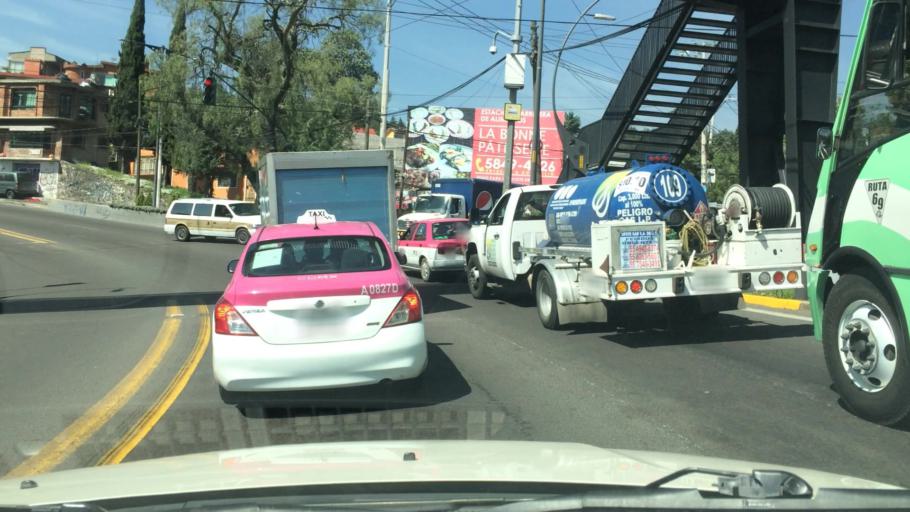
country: MX
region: Mexico City
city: Tlalpan
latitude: 19.2564
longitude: -99.1784
